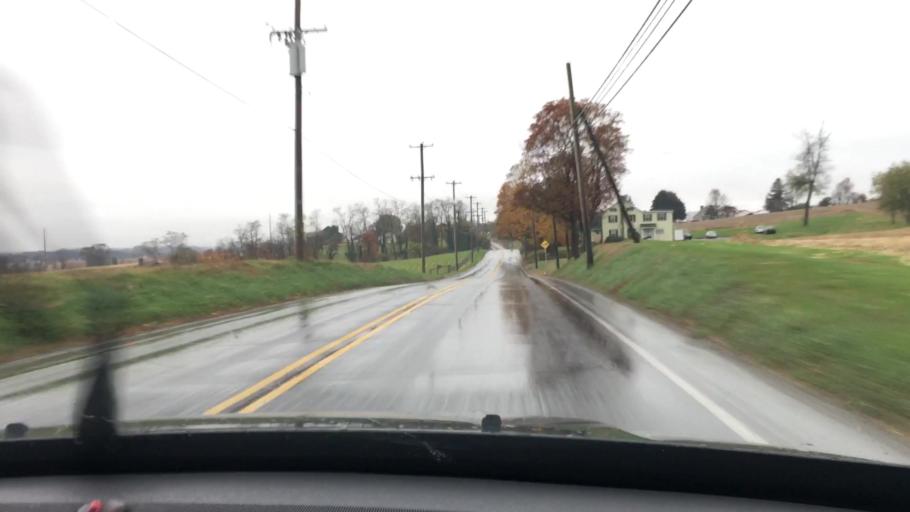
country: US
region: Pennsylvania
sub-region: York County
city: Susquehanna Trails
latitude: 39.8111
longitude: -76.3772
